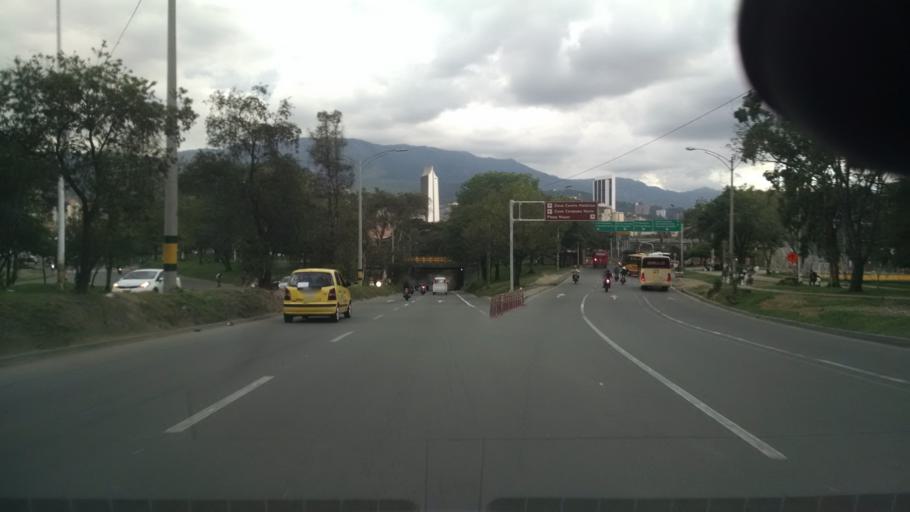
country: CO
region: Antioquia
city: Medellin
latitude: 6.2594
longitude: -75.5727
